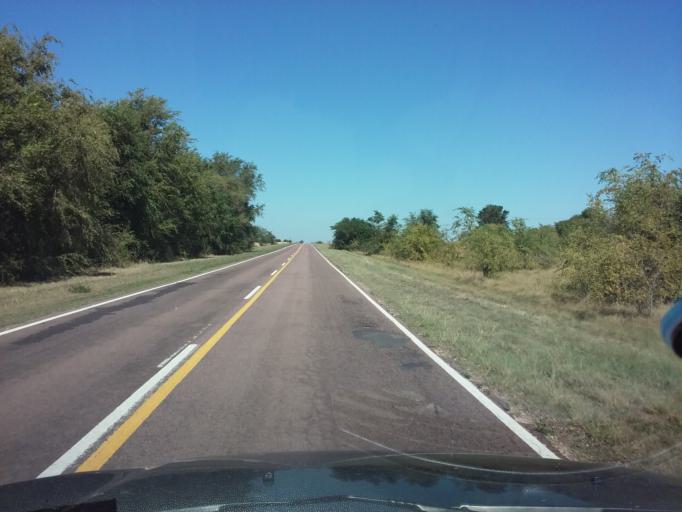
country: AR
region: La Pampa
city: Uriburu
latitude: -36.3800
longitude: -63.9431
